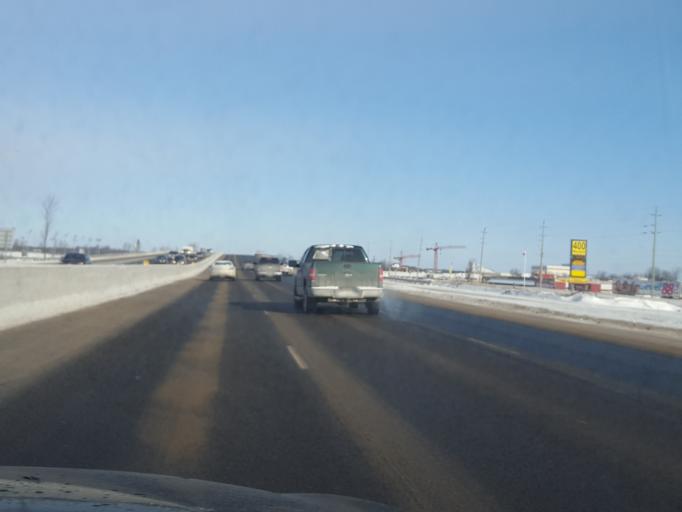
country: CA
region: Ontario
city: Innisfil
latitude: 44.2862
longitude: -79.6799
